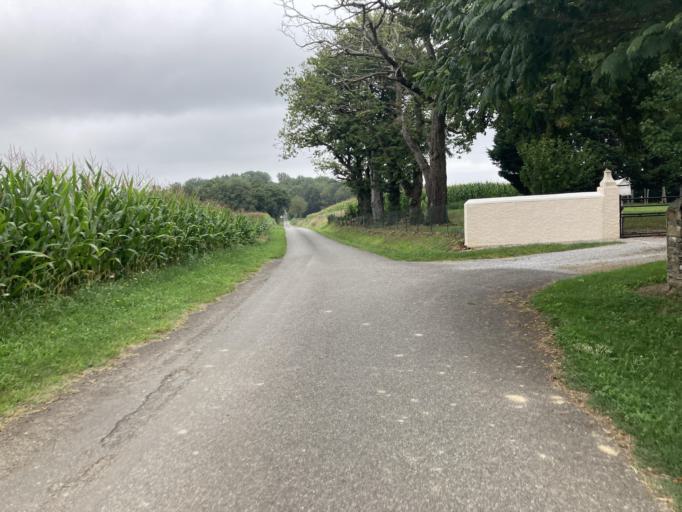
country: FR
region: Aquitaine
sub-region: Departement des Pyrenees-Atlantiques
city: Ledeuix
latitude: 43.2569
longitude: -0.6254
